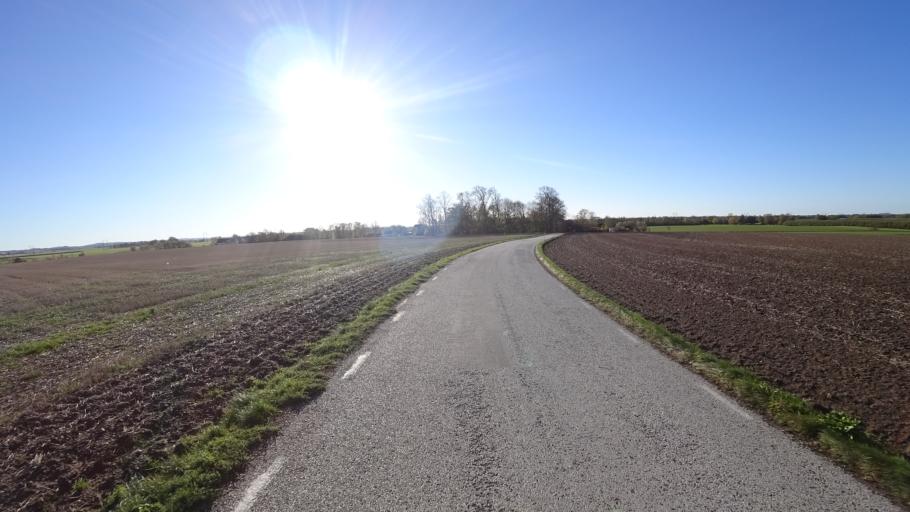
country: SE
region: Skane
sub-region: Staffanstorps Kommun
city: Staffanstorp
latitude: 55.6741
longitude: 13.2328
